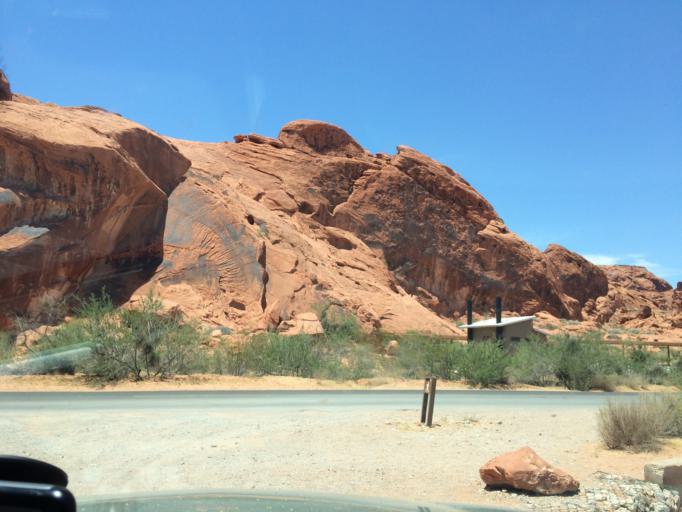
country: US
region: Nevada
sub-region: Clark County
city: Moapa Valley
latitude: 36.4411
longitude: -114.5165
